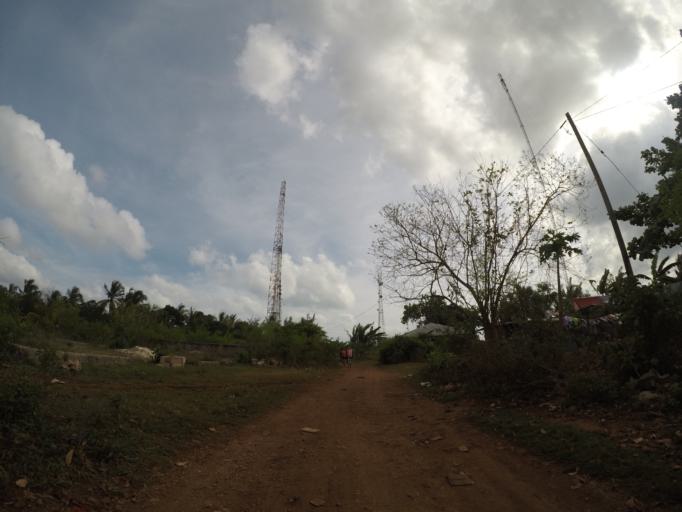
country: TZ
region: Zanzibar Central/South
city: Koani
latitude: -6.2227
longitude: 39.3191
